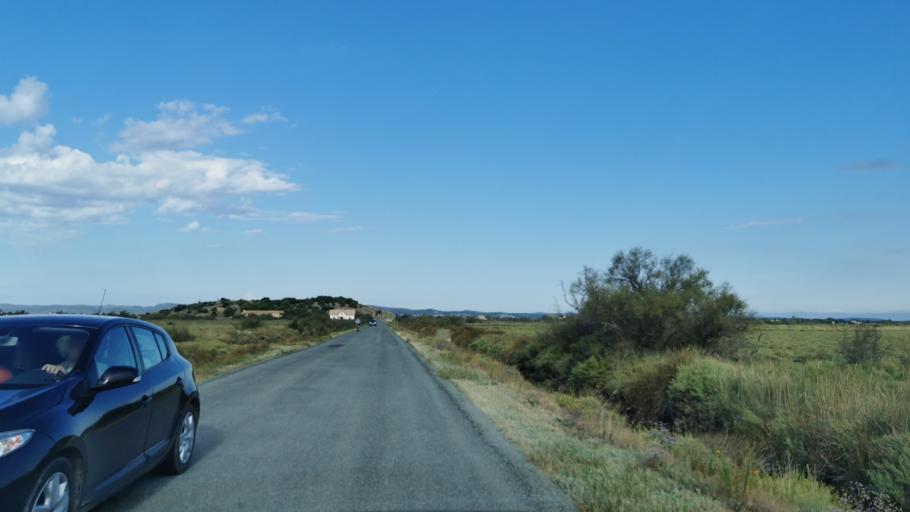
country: FR
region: Languedoc-Roussillon
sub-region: Departement de l'Aude
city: Gruissan
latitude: 43.1113
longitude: 3.0518
